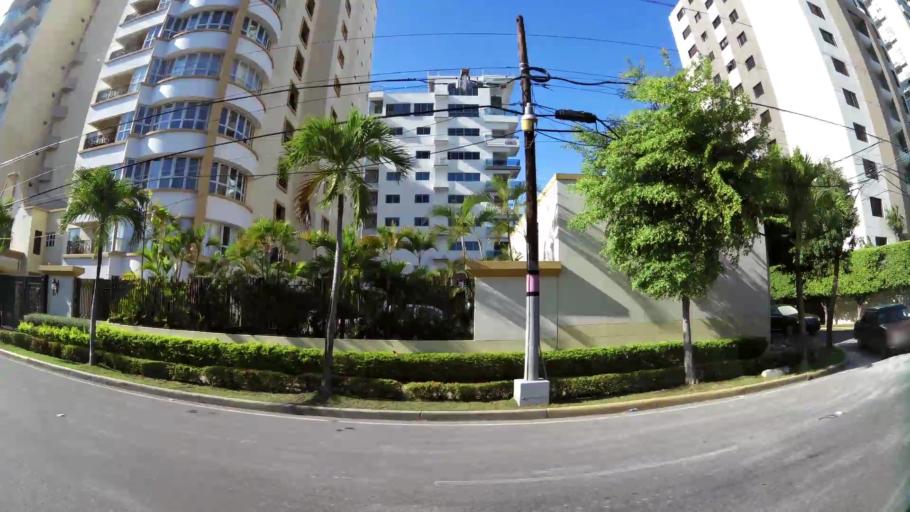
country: DO
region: Nacional
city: Bella Vista
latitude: 18.4370
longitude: -69.9762
